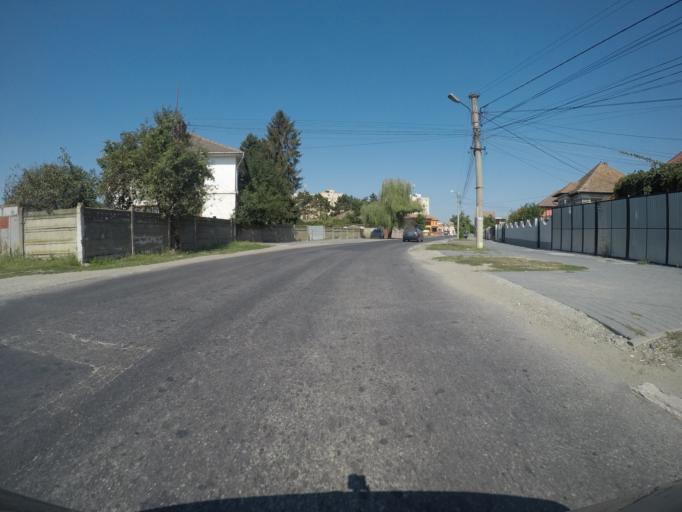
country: RO
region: Brasov
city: Fogarasch
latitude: 45.8296
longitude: 24.9776
